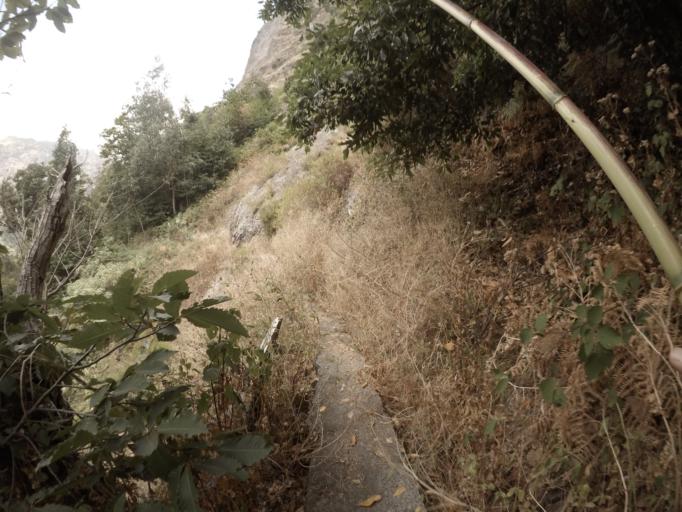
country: PT
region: Madeira
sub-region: Camara de Lobos
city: Curral das Freiras
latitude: 32.6999
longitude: -16.9698
